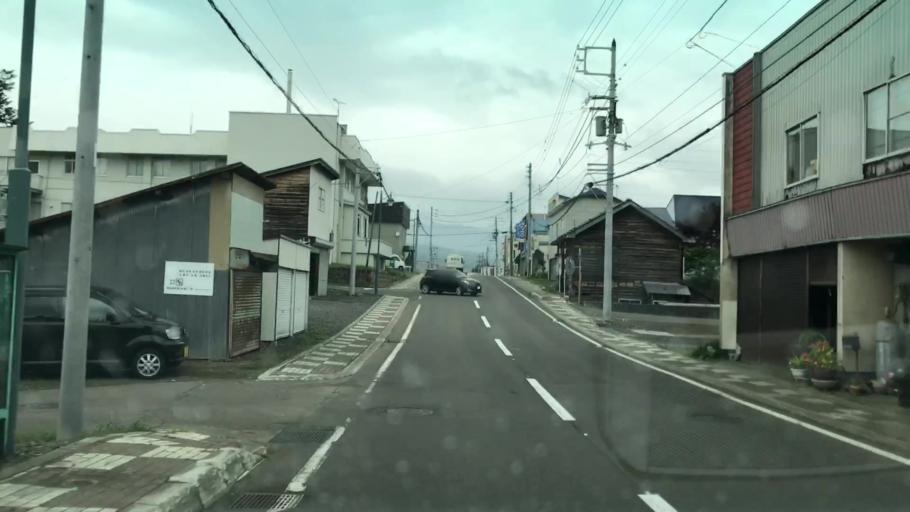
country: JP
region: Hokkaido
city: Niseko Town
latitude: 42.8037
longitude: 140.5266
